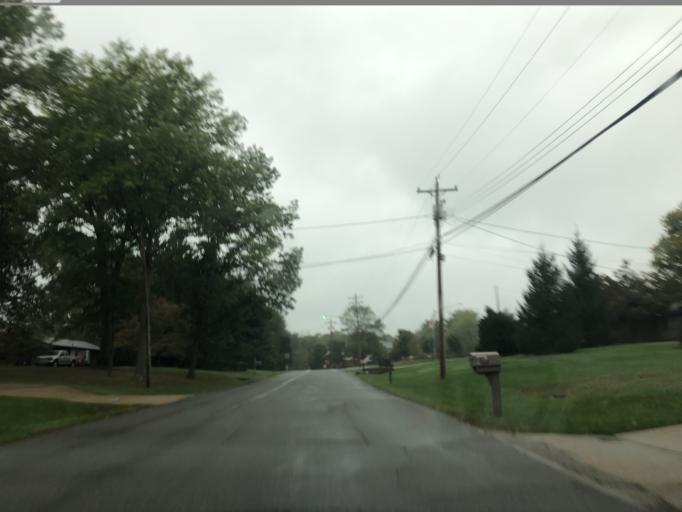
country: US
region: Ohio
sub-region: Hamilton County
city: Loveland
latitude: 39.2698
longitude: -84.2819
